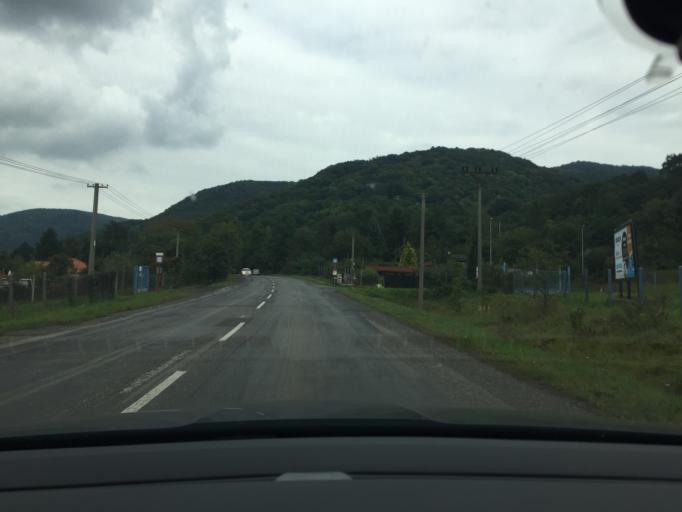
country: CZ
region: Ustecky
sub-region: Okres Usti nad Labem
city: Usti nad Labem
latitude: 50.5972
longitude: 14.0711
